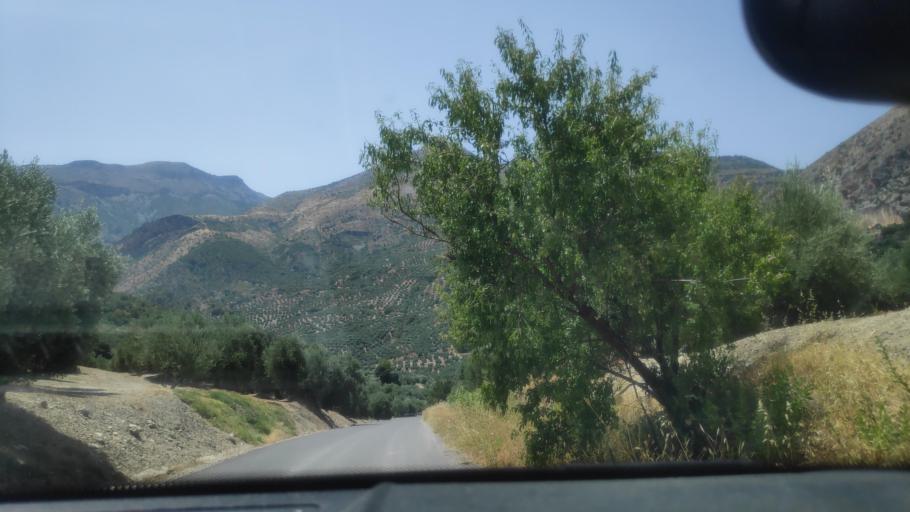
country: ES
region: Andalusia
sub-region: Provincia de Jaen
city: Jimena
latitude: 37.7910
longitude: -3.4527
